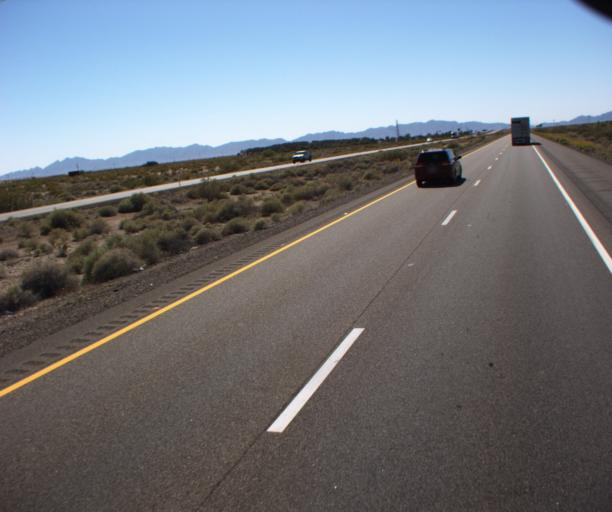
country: US
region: Arizona
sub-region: Yuma County
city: Wellton
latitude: 32.8049
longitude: -113.5302
